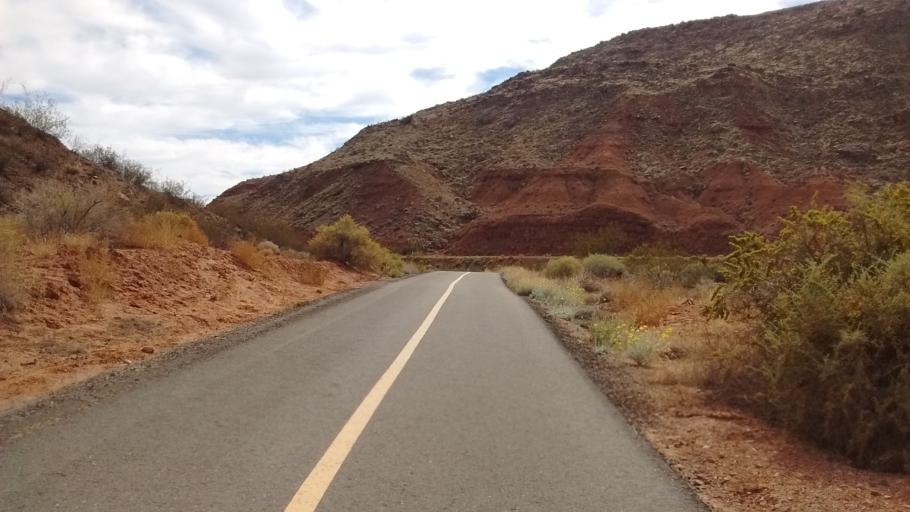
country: US
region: Utah
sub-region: Washington County
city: Washington
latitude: 37.1233
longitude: -113.4848
